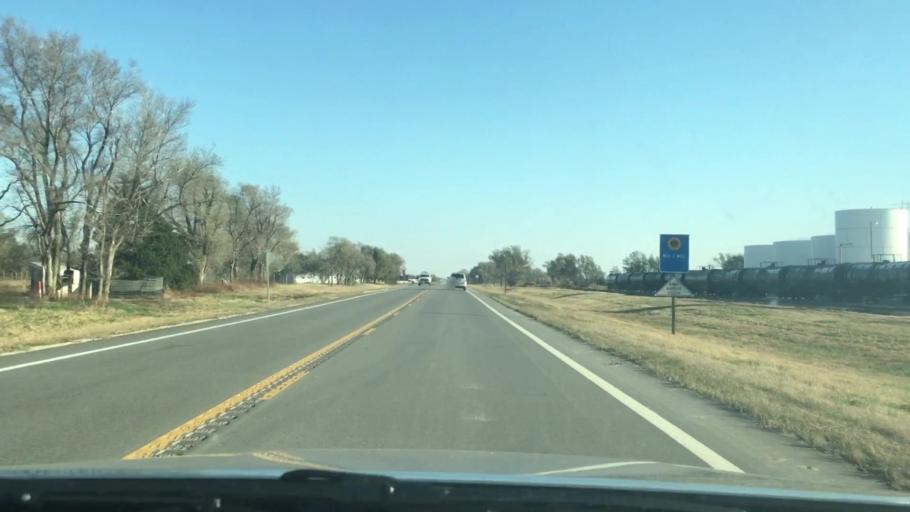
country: US
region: Kansas
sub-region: Reno County
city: Nickerson
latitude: 38.1434
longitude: -98.0780
